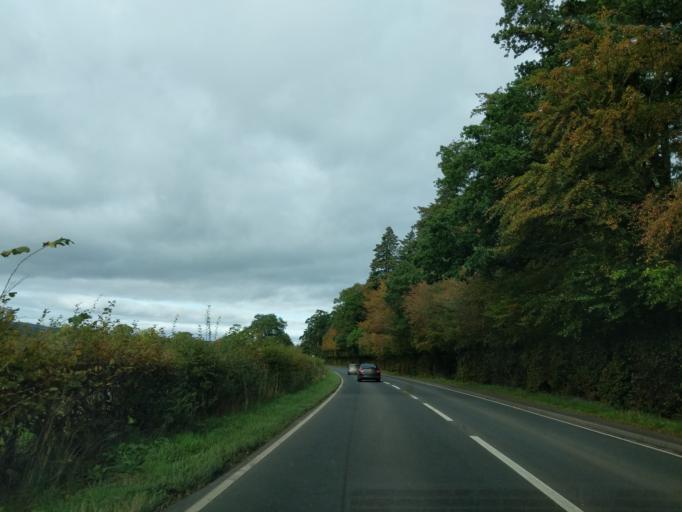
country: GB
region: Scotland
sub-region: Dumfries and Galloway
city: Thornhill
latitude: 55.2574
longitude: -3.7757
